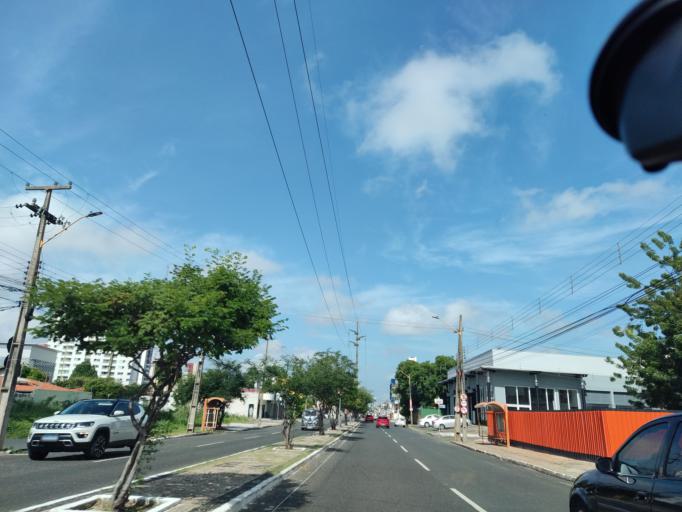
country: BR
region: Piaui
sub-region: Teresina
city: Teresina
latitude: -5.0701
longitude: -42.7773
